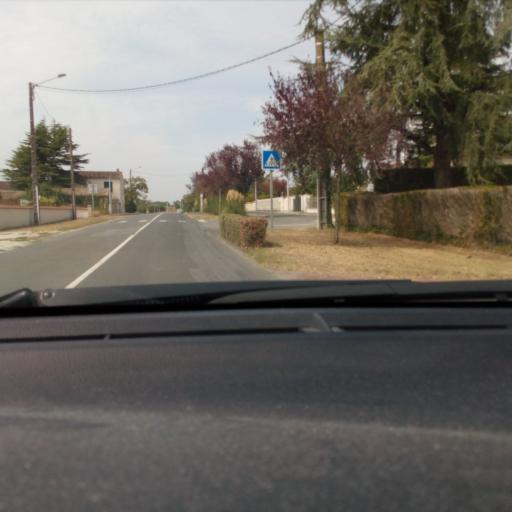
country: FR
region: Poitou-Charentes
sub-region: Departement de la Charente
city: Saint-Yrieix-sur-Charente
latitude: 45.6841
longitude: 0.1125
